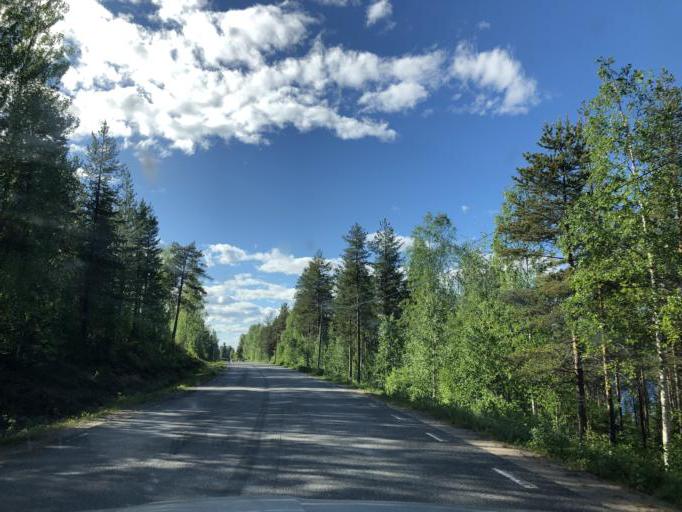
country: SE
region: Norrbotten
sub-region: Overkalix Kommun
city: OEverkalix
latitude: 66.3177
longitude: 22.8709
